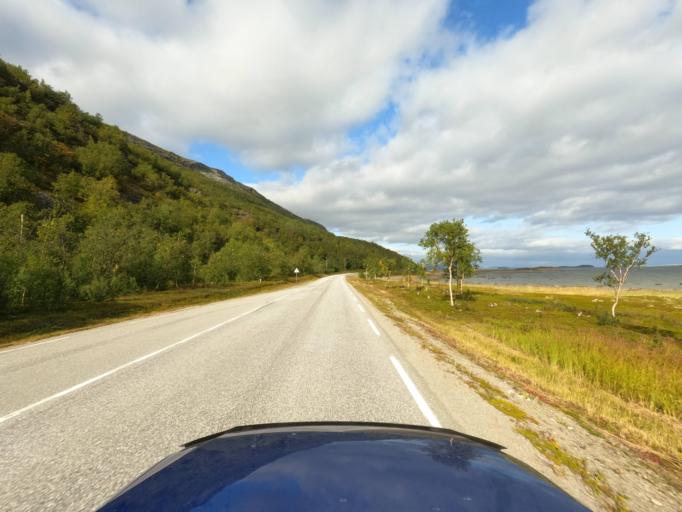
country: NO
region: Finnmark Fylke
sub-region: Porsanger
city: Lakselv
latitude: 70.1067
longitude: 24.9177
